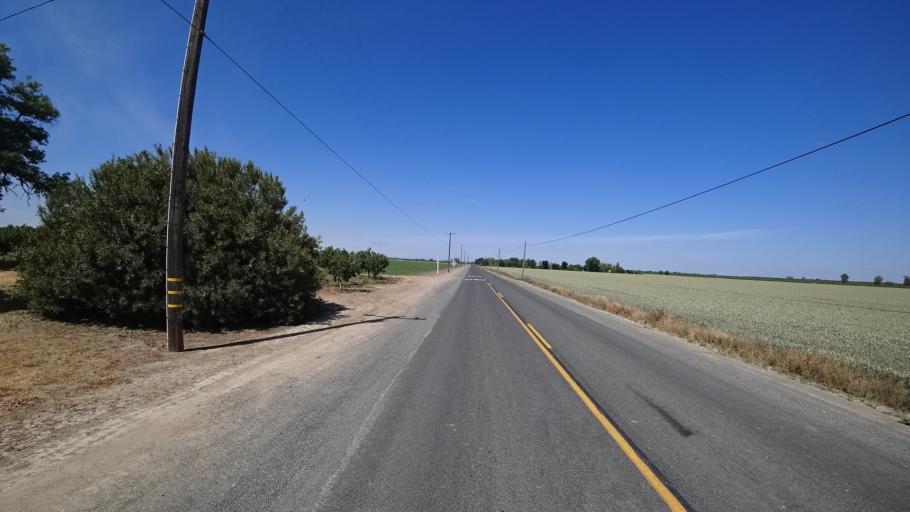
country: US
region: California
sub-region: Kings County
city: Armona
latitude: 36.2693
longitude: -119.7102
